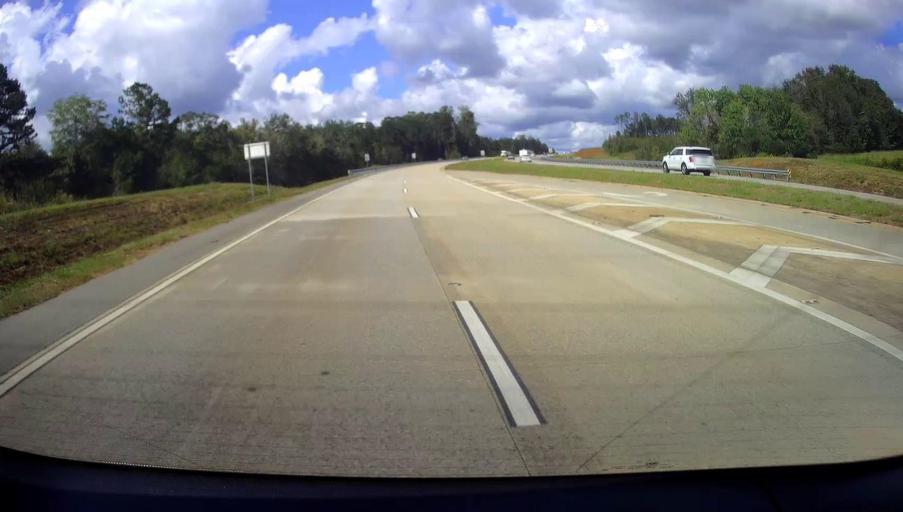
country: US
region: Georgia
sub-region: Jones County
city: Gray
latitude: 32.9922
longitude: -83.5738
